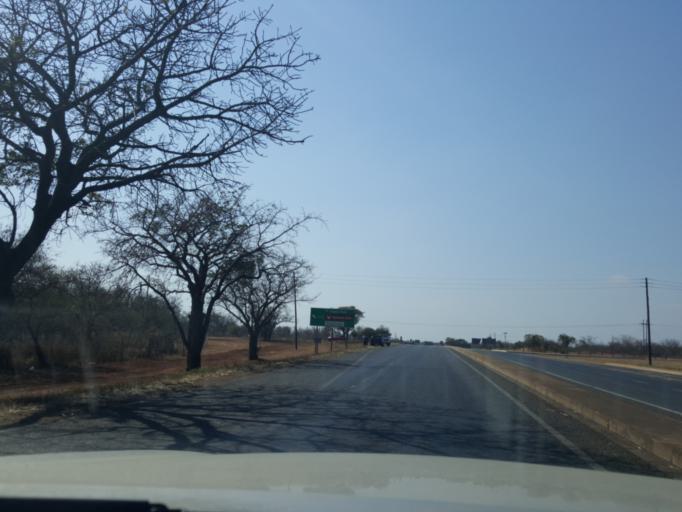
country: SZ
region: Hhohho
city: Ntfonjeni
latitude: -25.4822
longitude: 31.5466
